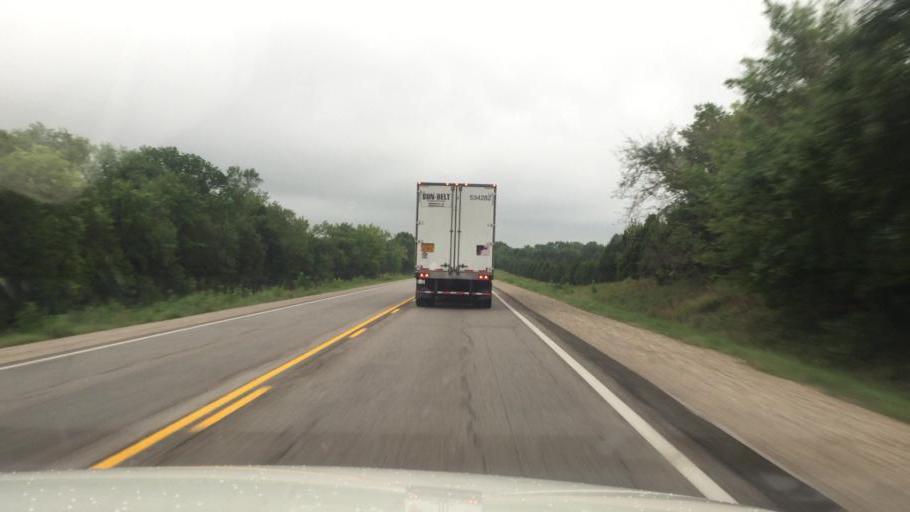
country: US
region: Kansas
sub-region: Montgomery County
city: Coffeyville
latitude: 37.1477
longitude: -95.5769
